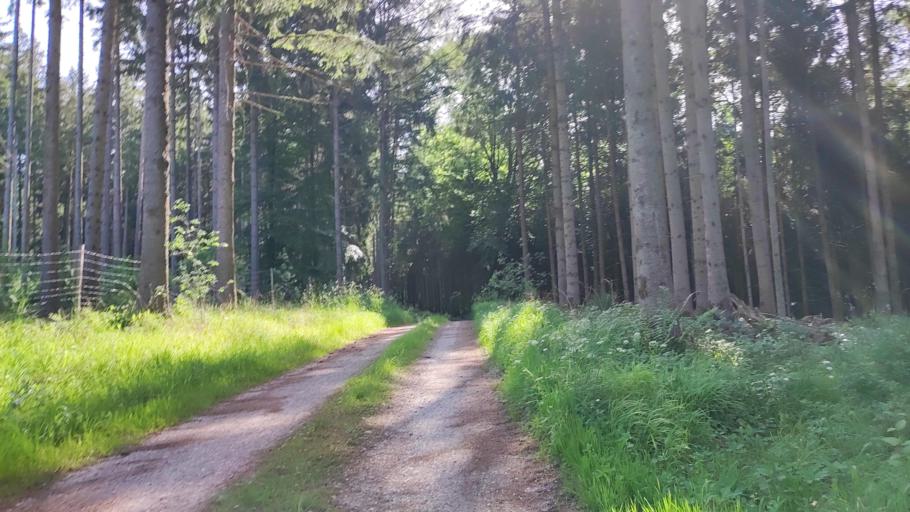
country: DE
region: Bavaria
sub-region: Swabia
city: Landensberg
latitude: 48.4143
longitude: 10.5521
